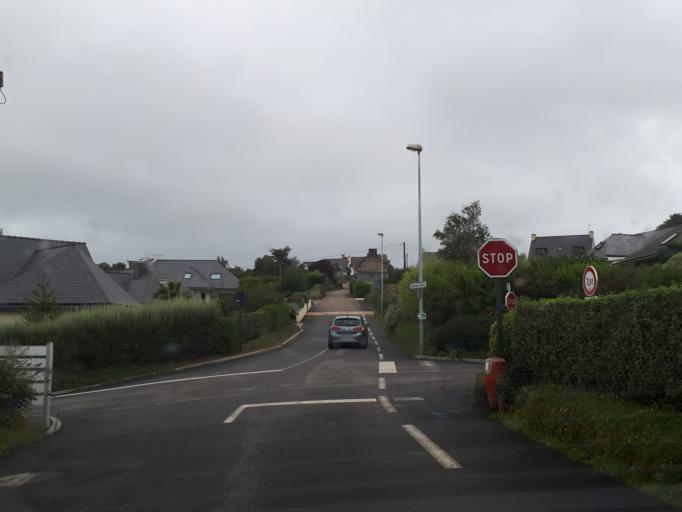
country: FR
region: Brittany
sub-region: Departement du Finistere
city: Carantec
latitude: 48.6597
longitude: -3.9258
